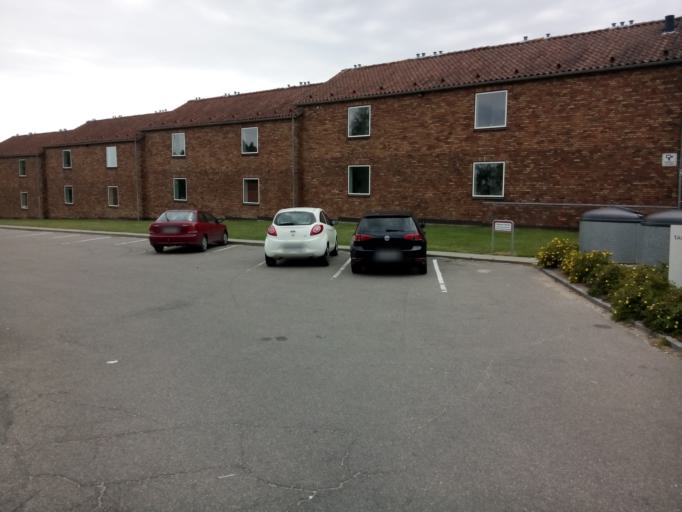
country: DK
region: Central Jutland
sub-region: Arhus Kommune
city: Arhus
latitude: 56.1653
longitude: 10.1831
